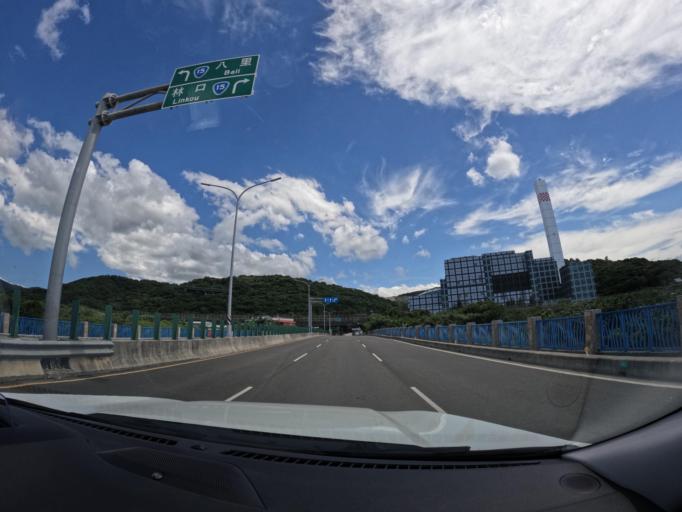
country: TW
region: Taiwan
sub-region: Taoyuan
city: Taoyuan
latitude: 25.1376
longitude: 121.3678
